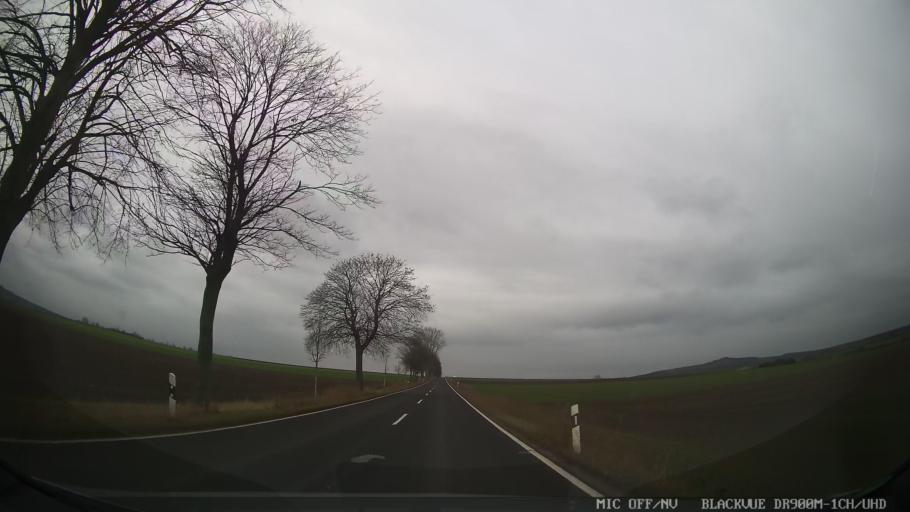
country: DE
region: Rheinland-Pfalz
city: Frettenheim
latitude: 49.7739
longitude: 8.2309
